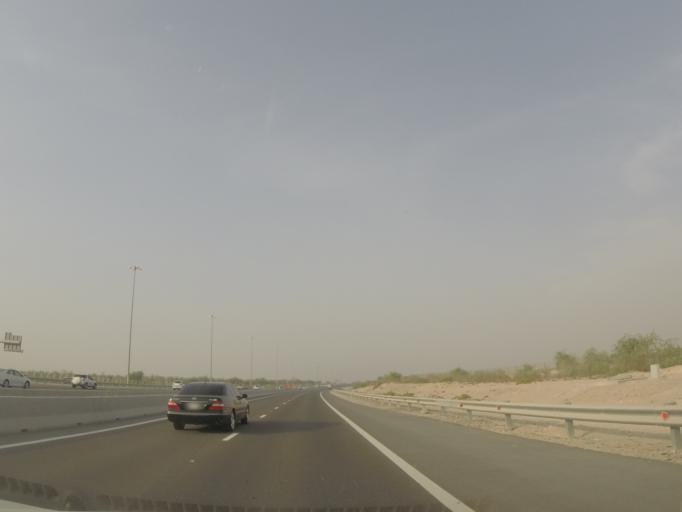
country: AE
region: Abu Dhabi
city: Abu Dhabi
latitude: 24.7006
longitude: 54.7847
